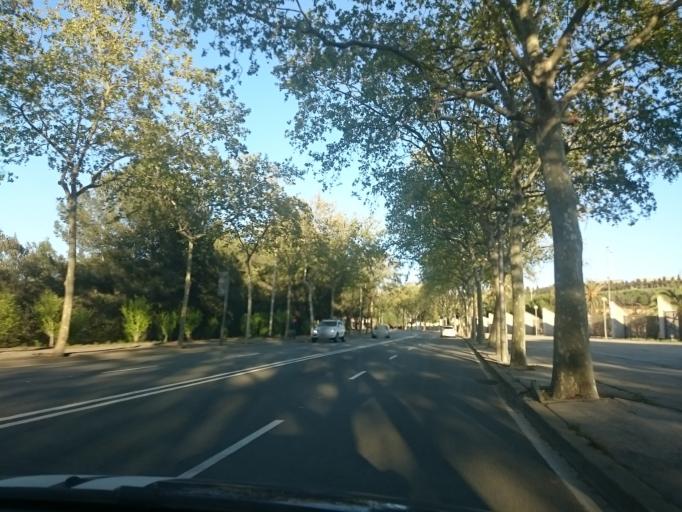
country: ES
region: Catalonia
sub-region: Provincia de Barcelona
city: Sants-Montjuic
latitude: 41.3599
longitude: 2.1474
